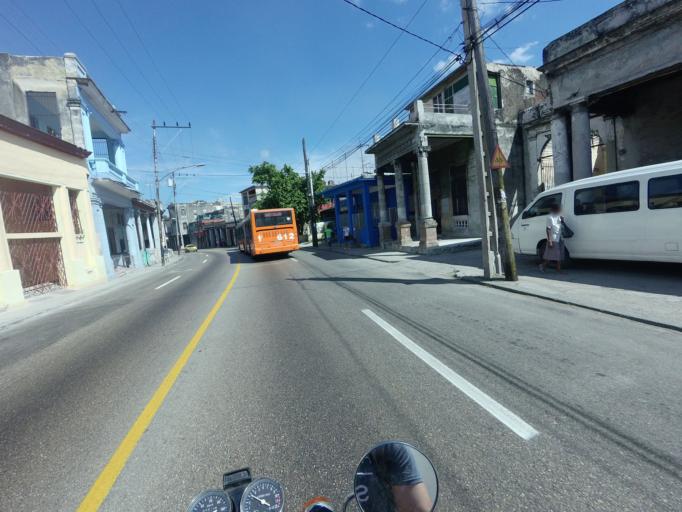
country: CU
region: La Habana
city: Diez de Octubre
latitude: 23.1012
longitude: -82.3629
